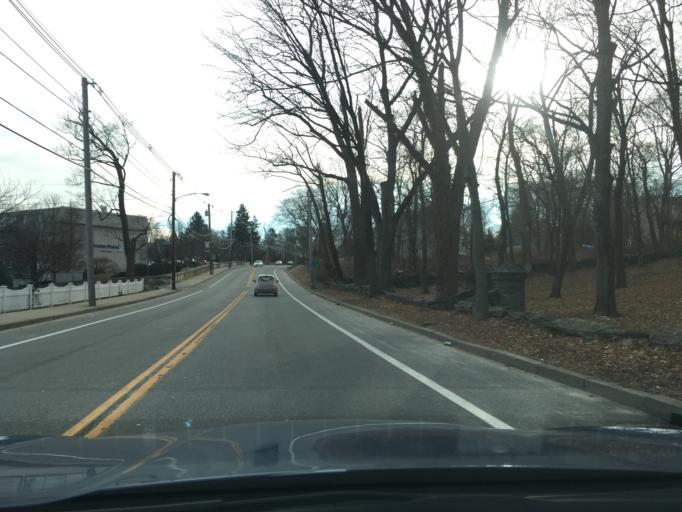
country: US
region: Rhode Island
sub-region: Kent County
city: East Greenwich
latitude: 41.6717
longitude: -71.4481
